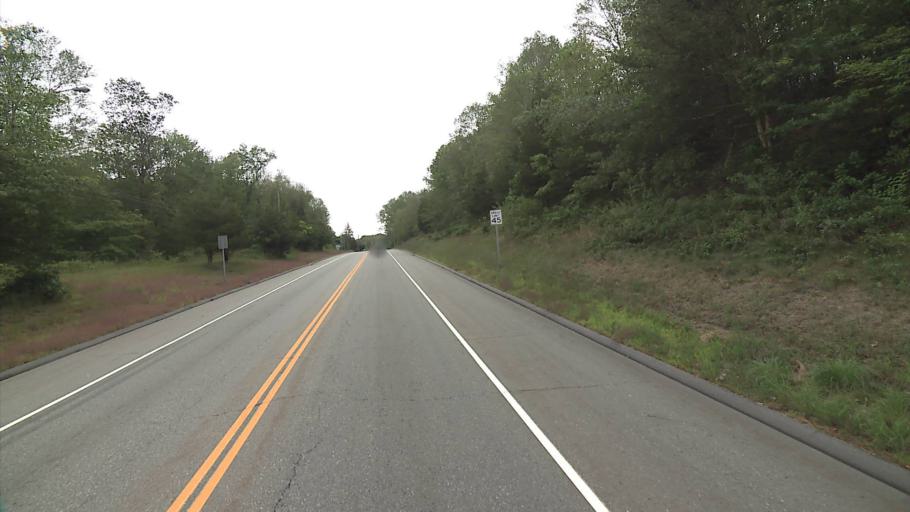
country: US
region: Connecticut
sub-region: New London County
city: Montville Center
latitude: 41.4269
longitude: -72.2128
